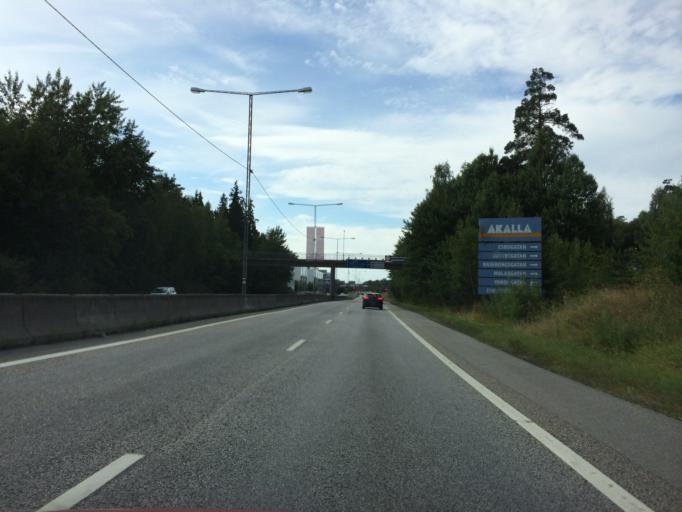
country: SE
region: Stockholm
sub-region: Stockholms Kommun
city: Kista
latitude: 59.4155
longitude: 17.9276
